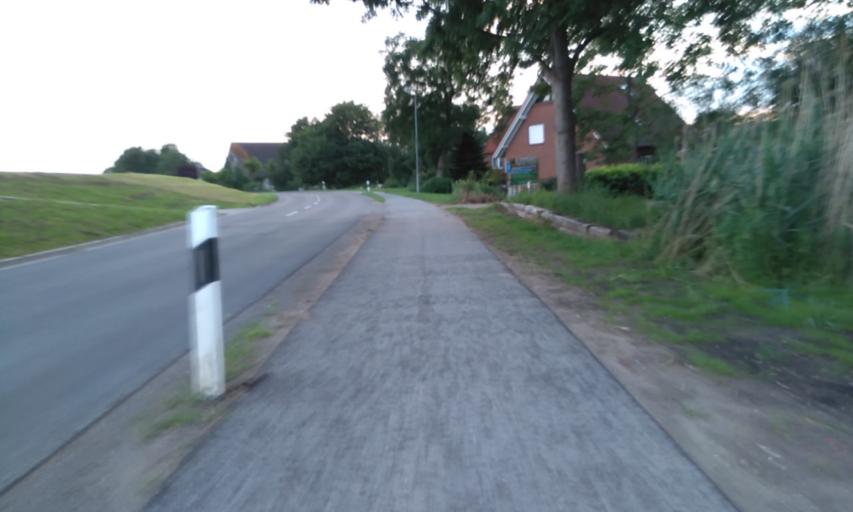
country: DE
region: Lower Saxony
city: Buxtehude
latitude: 53.4879
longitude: 9.7083
